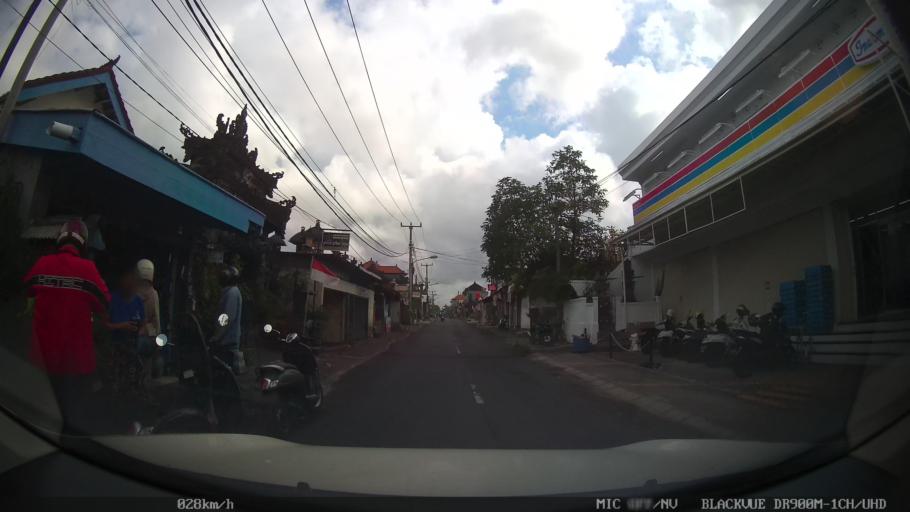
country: ID
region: Bali
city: Banjar Kertasari
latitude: -8.6228
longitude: 115.2026
